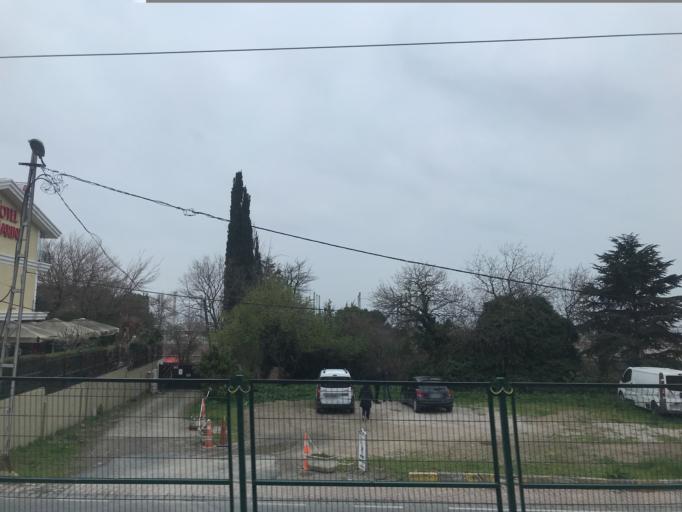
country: TR
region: Istanbul
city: Pendik
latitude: 40.8745
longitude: 29.2489
